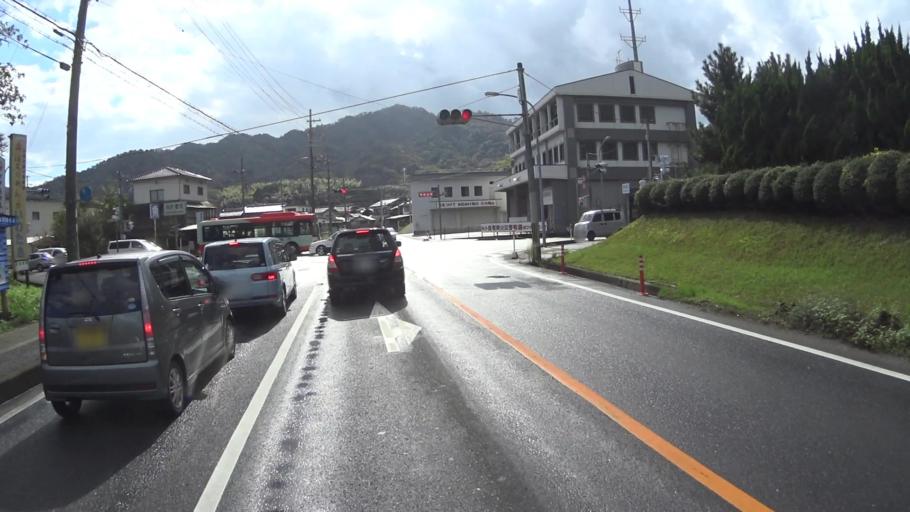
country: JP
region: Kyoto
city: Miyazu
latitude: 35.5535
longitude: 135.1507
